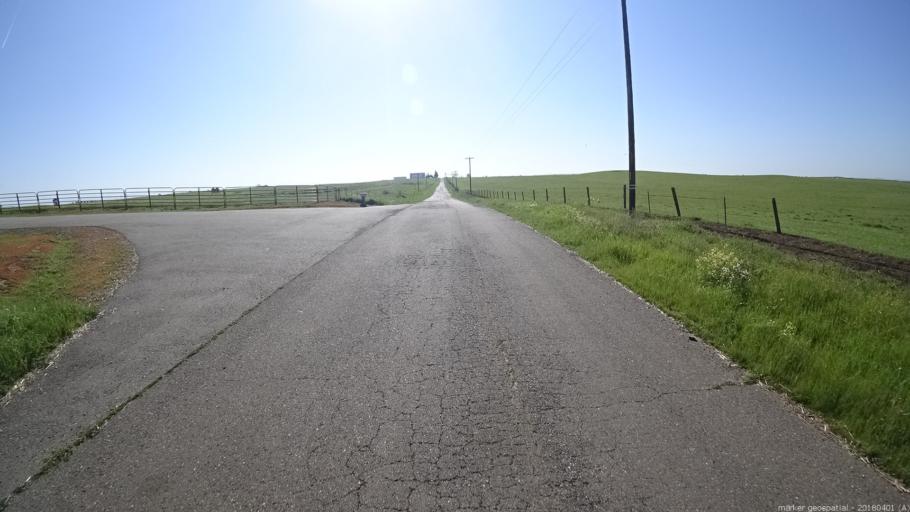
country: US
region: California
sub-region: Sacramento County
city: Rancho Murieta
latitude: 38.4798
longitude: -121.1806
